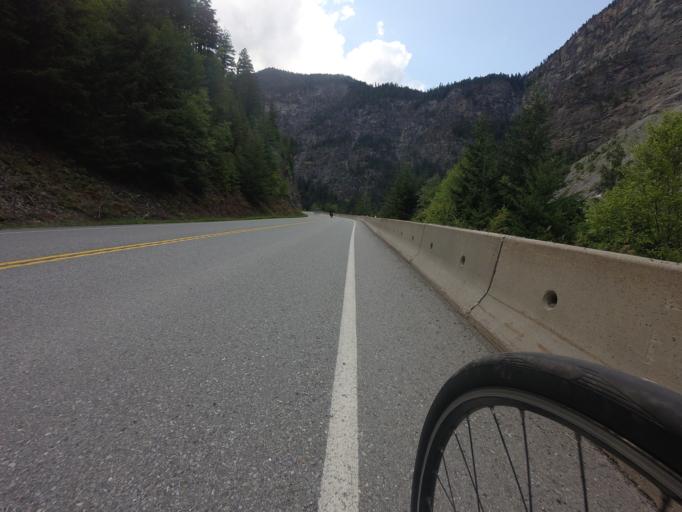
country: CA
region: British Columbia
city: Lillooet
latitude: 50.6457
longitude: -122.0629
